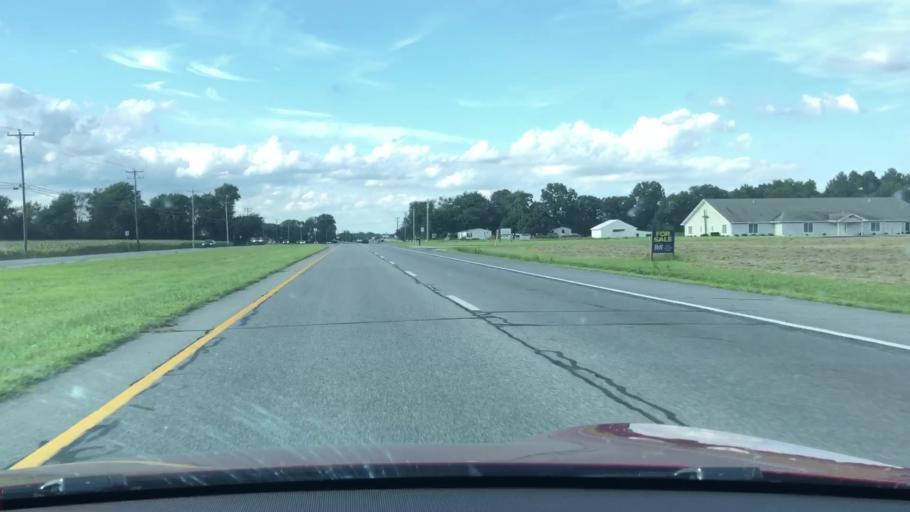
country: US
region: Delaware
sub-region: Kent County
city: Felton
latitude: 38.9873
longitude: -75.5676
